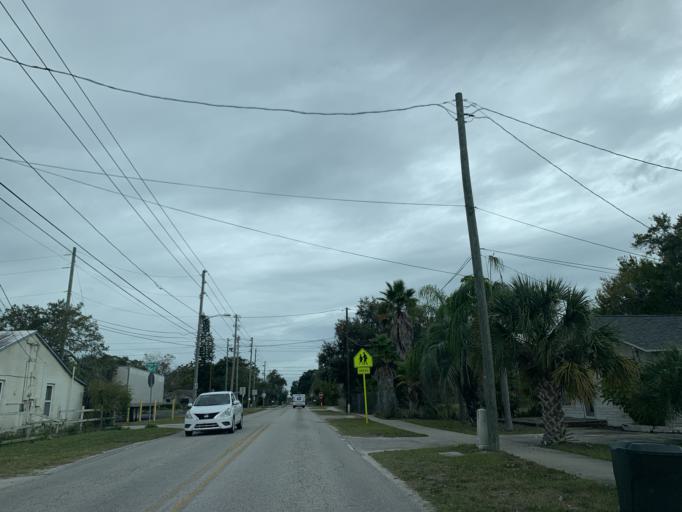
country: US
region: Florida
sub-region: Pinellas County
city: Belleair
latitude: 27.9352
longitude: -82.7906
